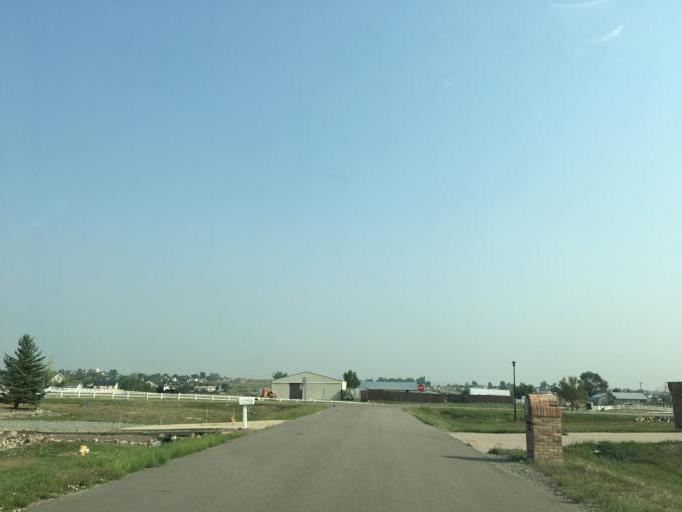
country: US
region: Colorado
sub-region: Adams County
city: Todd Creek
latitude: 39.9749
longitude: -104.8670
